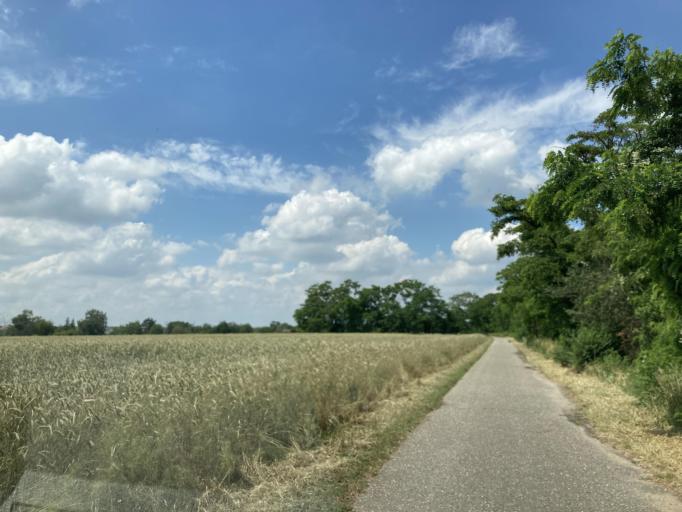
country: DE
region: Baden-Wuerttemberg
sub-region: Karlsruhe Region
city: Waghausel
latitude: 49.2607
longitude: 8.4971
